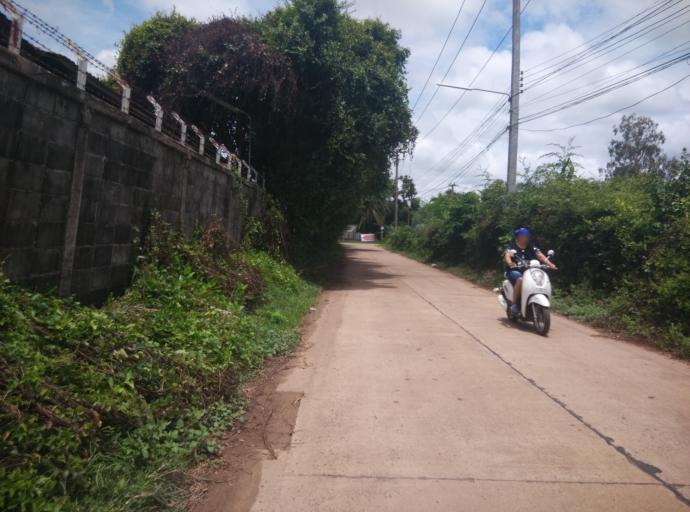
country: TH
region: Sisaket
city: Si Sa Ket
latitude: 15.1094
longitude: 104.3591
